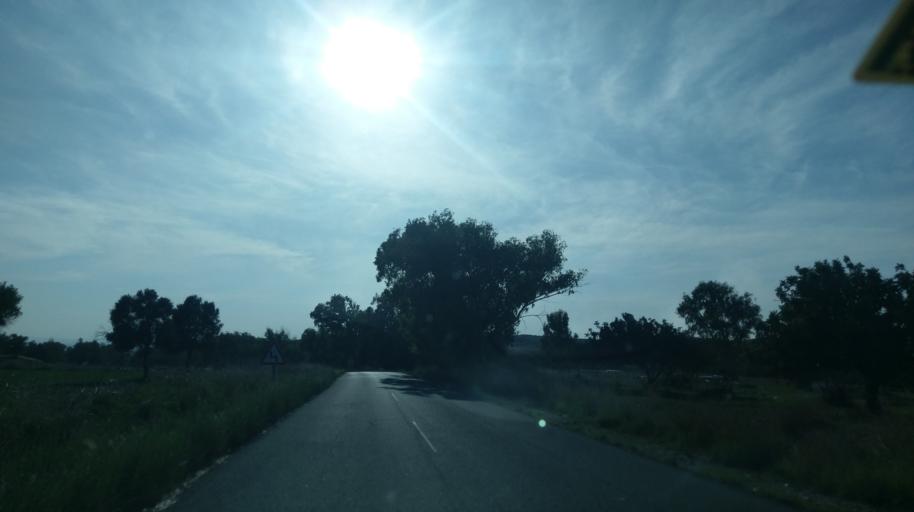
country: CY
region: Ammochostos
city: Lefkonoiko
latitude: 35.2960
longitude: 33.7396
